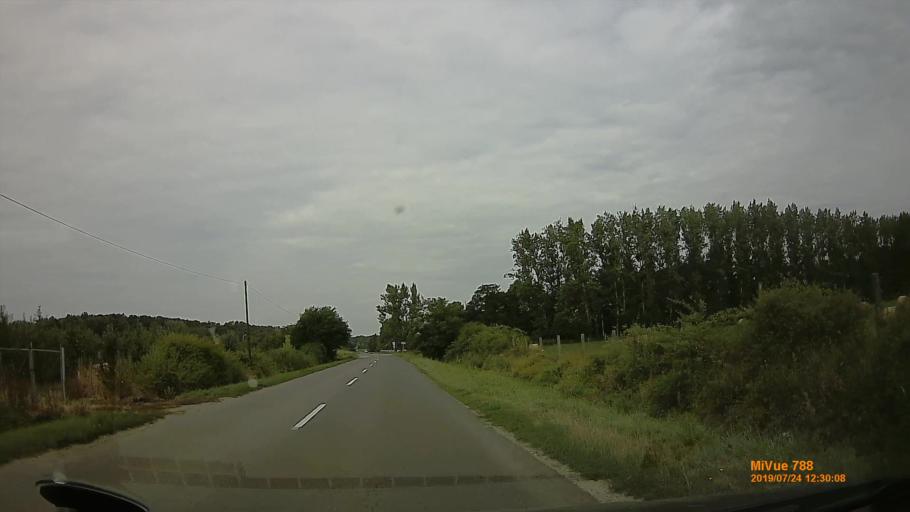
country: HU
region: Szabolcs-Szatmar-Bereg
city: Vasarosnameny
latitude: 48.1613
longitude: 22.3413
